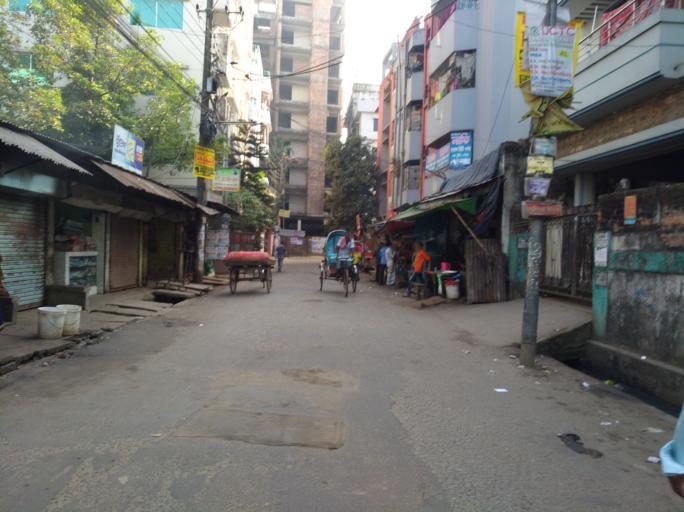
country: BD
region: Chittagong
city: Chittagong
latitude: 22.3581
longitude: 91.8172
